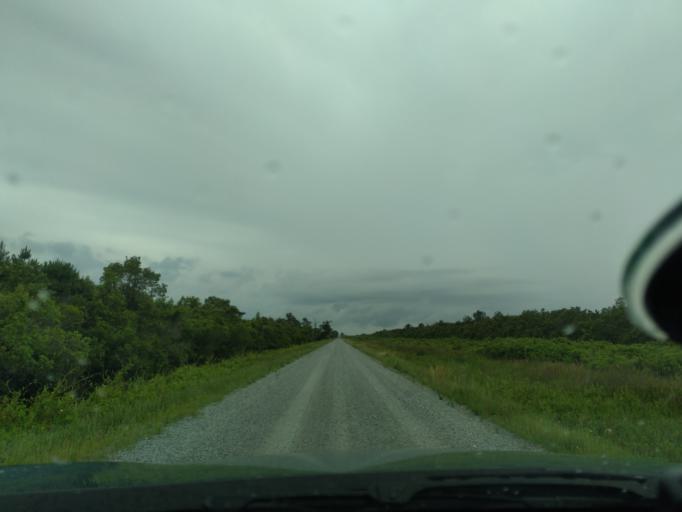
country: US
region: North Carolina
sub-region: Beaufort County
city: Belhaven
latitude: 35.7284
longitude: -76.4437
